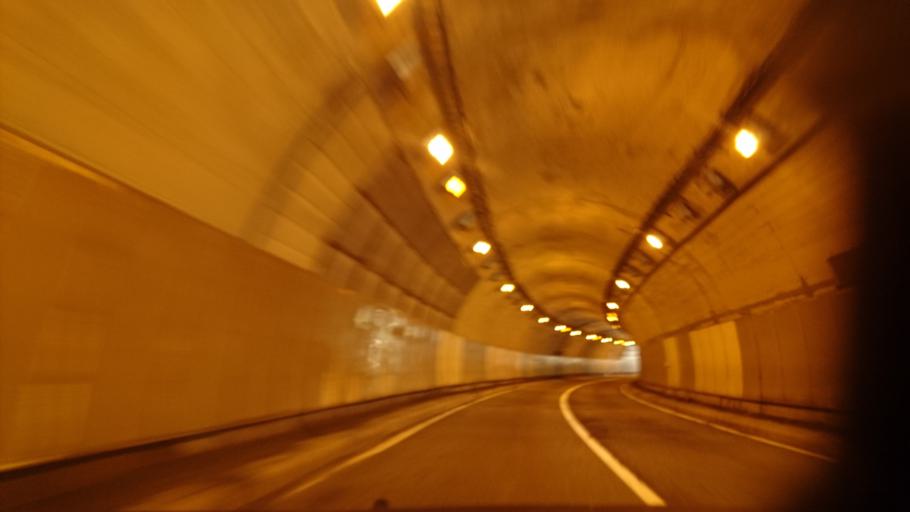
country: JP
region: Iwate
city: Shizukuishi
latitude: 39.6960
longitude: 140.7780
